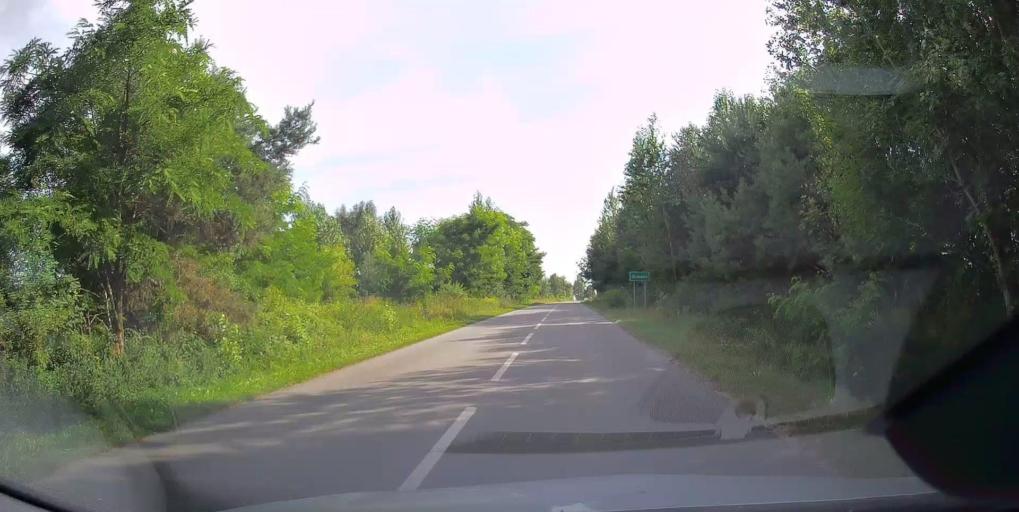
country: PL
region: Lodz Voivodeship
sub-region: Powiat opoczynski
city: Mniszkow
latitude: 51.3902
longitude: 20.0352
